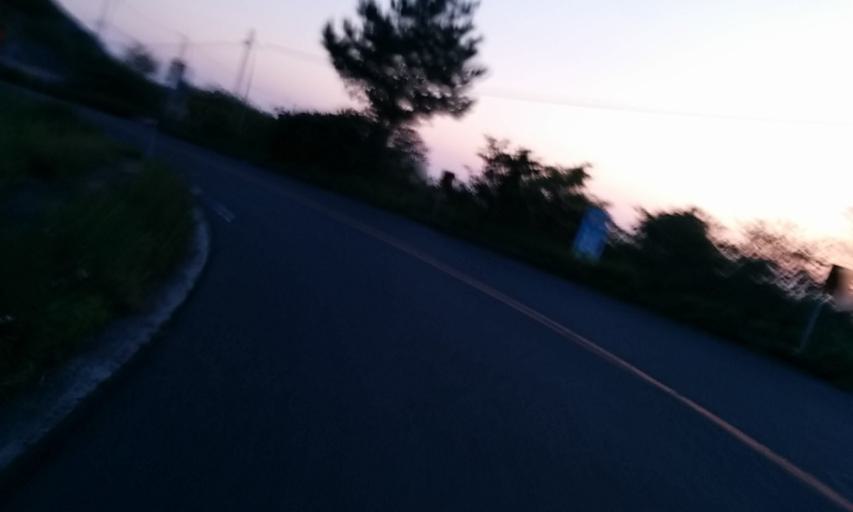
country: JP
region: Ehime
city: Ozu
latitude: 33.6005
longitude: 132.4654
